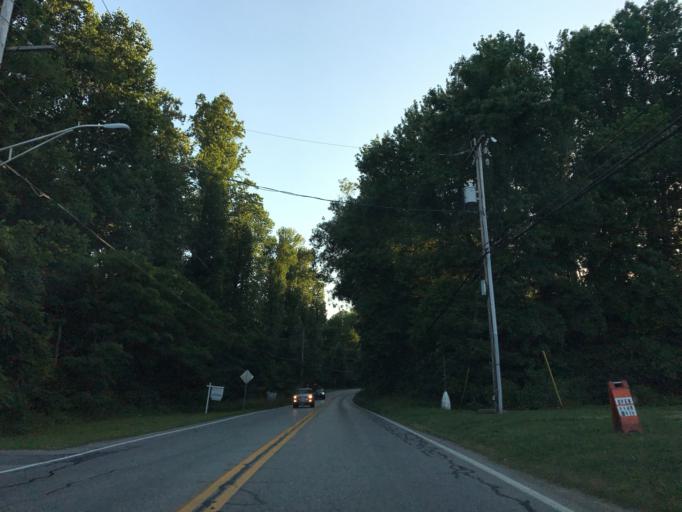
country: US
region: Maryland
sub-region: Anne Arundel County
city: Selby-on-the-Bay
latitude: 38.9061
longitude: -76.5277
